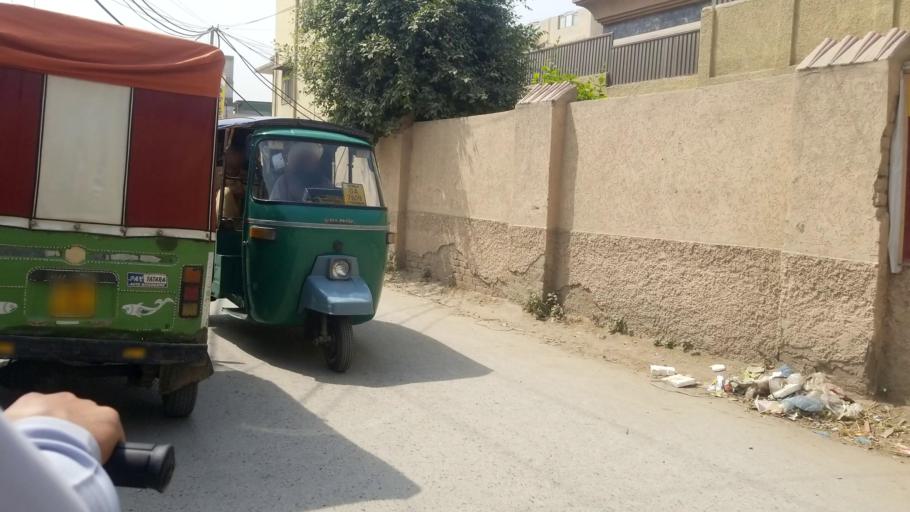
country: PK
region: Khyber Pakhtunkhwa
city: Peshawar
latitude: 33.9853
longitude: 71.5347
